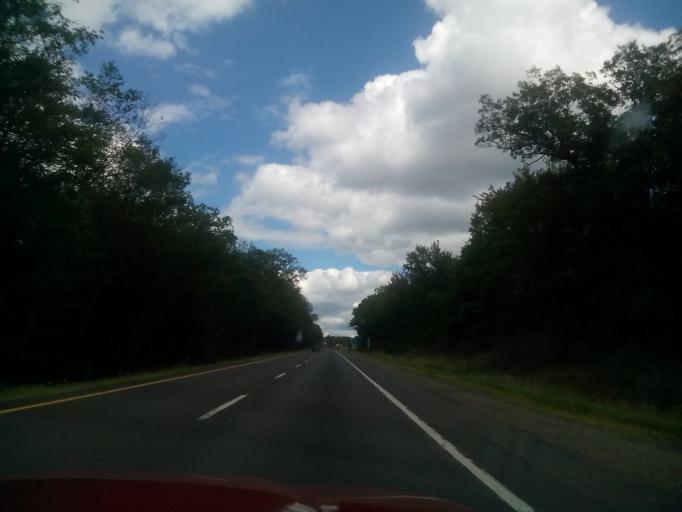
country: US
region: Pennsylvania
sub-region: Luzerne County
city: White Haven
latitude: 41.0612
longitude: -75.7115
